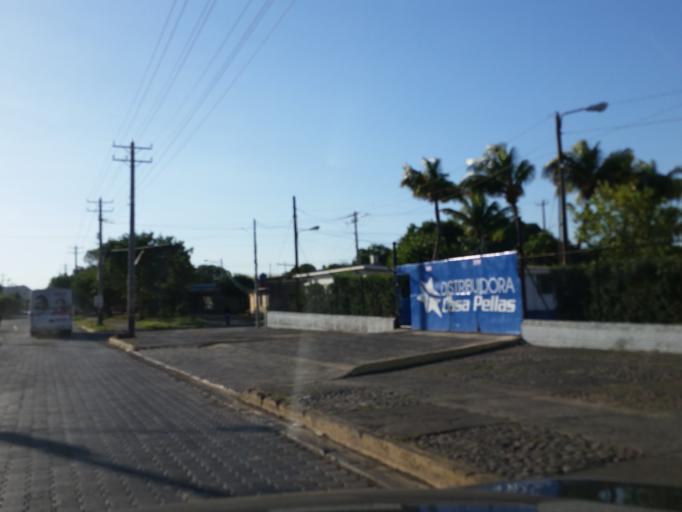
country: NI
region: Managua
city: Ciudad Sandino
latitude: 12.1581
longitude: -86.3011
